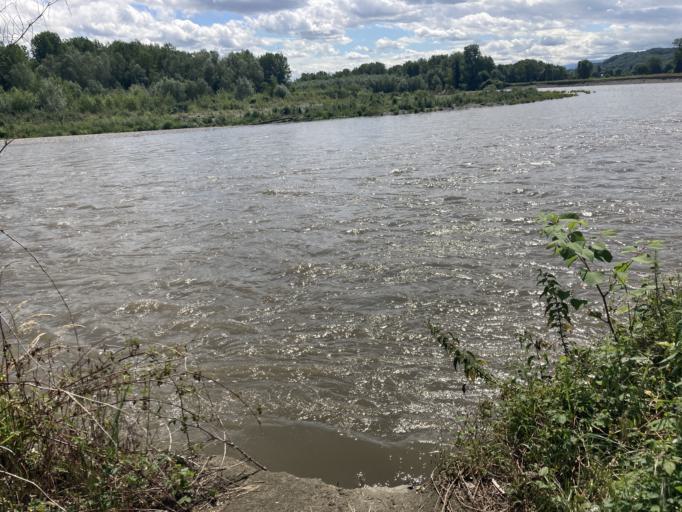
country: FR
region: Aquitaine
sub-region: Departement des Pyrenees-Atlantiques
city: Arbus
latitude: 43.3381
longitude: -0.4954
